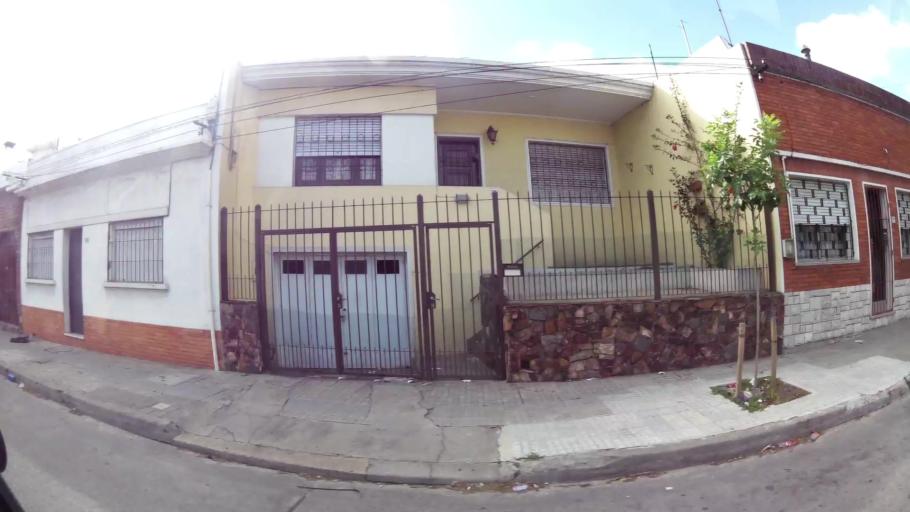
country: UY
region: Montevideo
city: Montevideo
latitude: -34.8813
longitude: -56.1582
